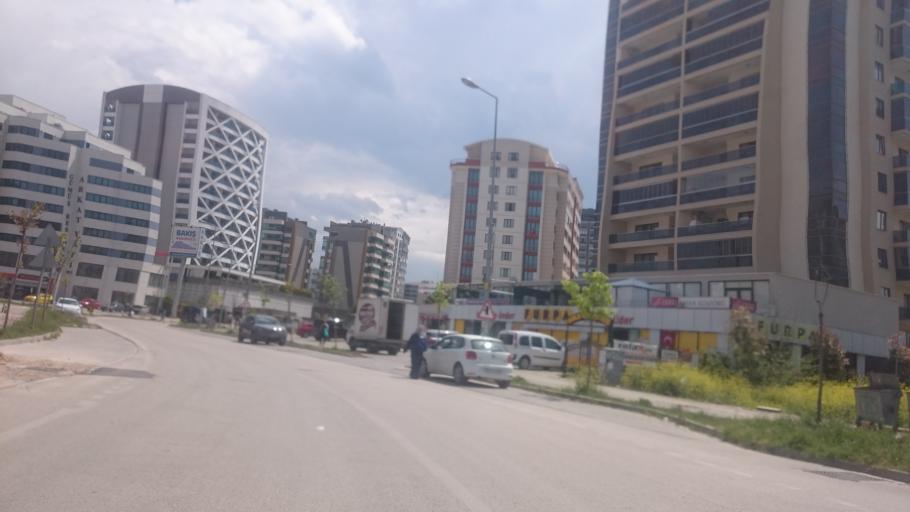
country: TR
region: Bursa
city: Cali
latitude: 40.2203
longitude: 28.9447
